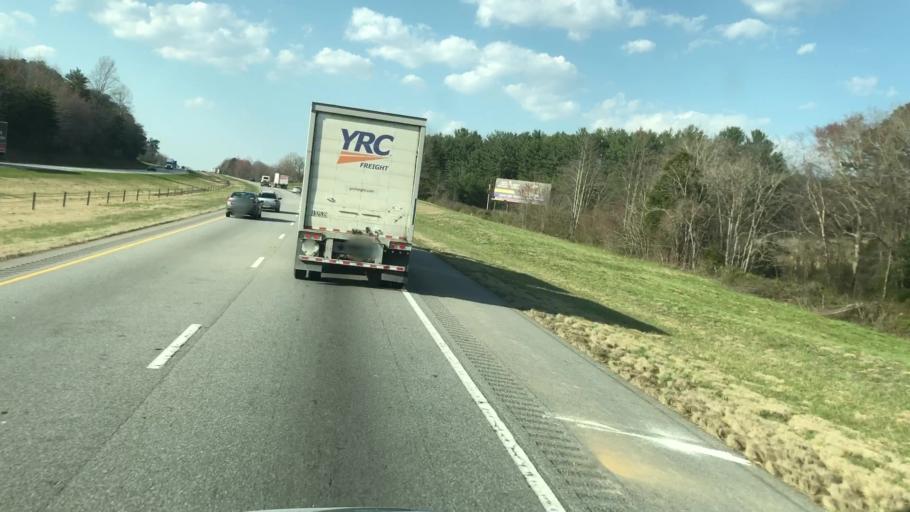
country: US
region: North Carolina
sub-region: Yadkin County
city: Yadkinville
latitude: 36.0344
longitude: -80.8186
